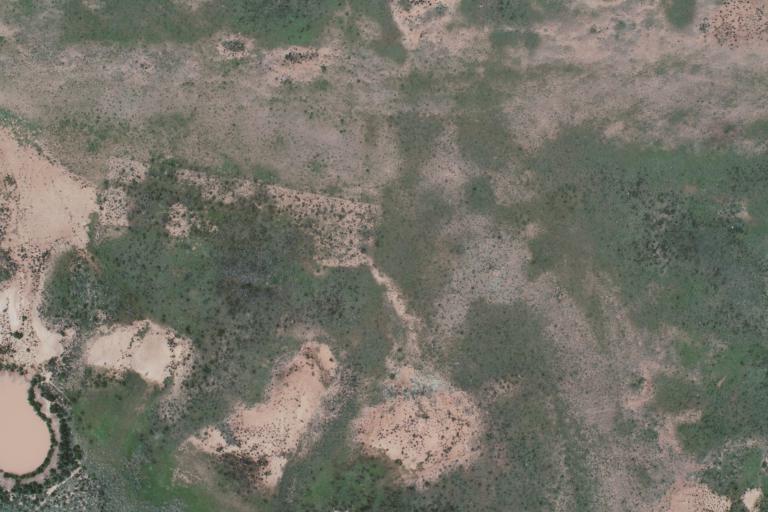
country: BO
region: La Paz
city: Curahuara de Carangas
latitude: -17.2925
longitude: -68.5005
